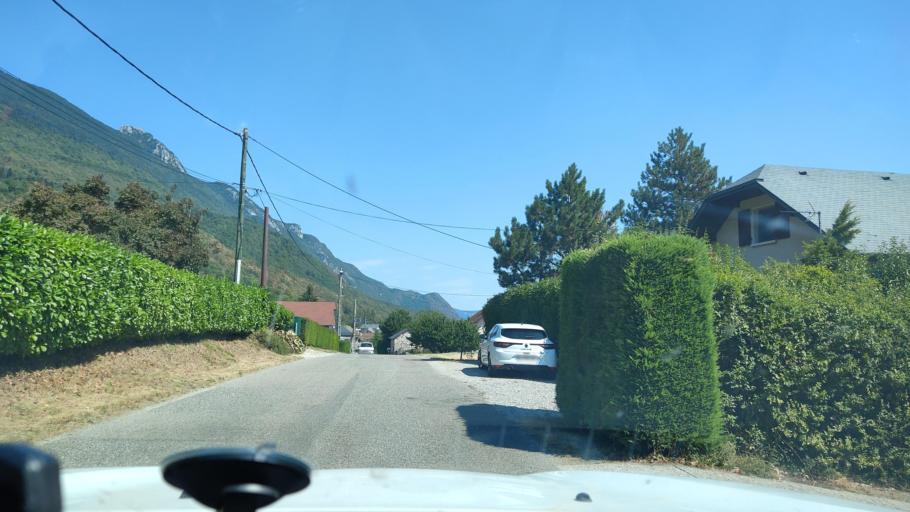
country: FR
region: Rhone-Alpes
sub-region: Departement de la Savoie
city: Le Bourget-du-Lac
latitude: 45.6420
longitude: 5.8492
